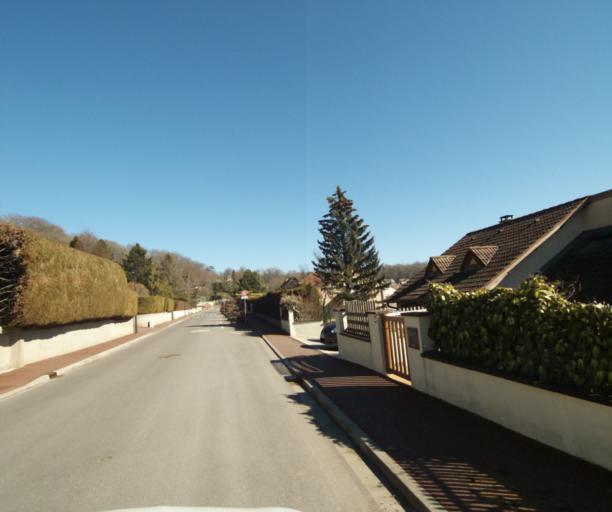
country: FR
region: Lorraine
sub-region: Departement de Meurthe-et-Moselle
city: Saint-Max
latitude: 48.7157
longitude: 6.2148
